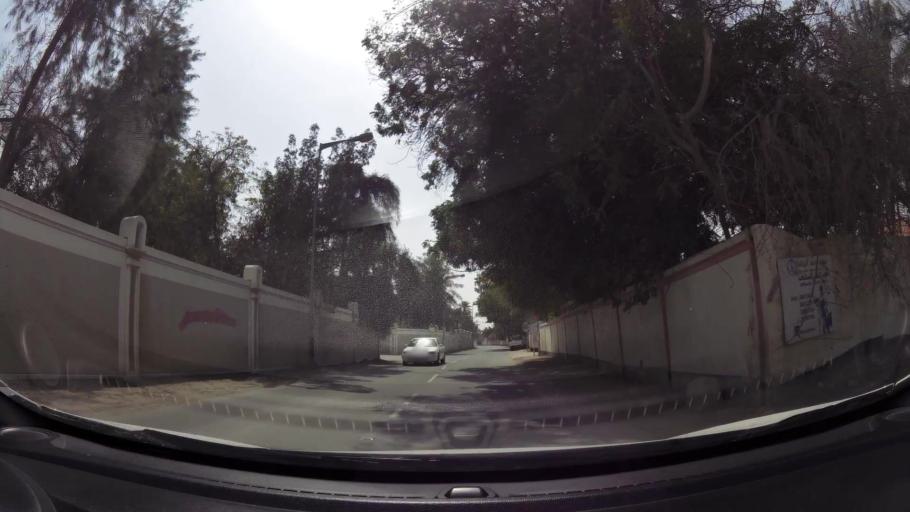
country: BH
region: Manama
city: Jidd Hafs
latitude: 26.2289
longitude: 50.5029
